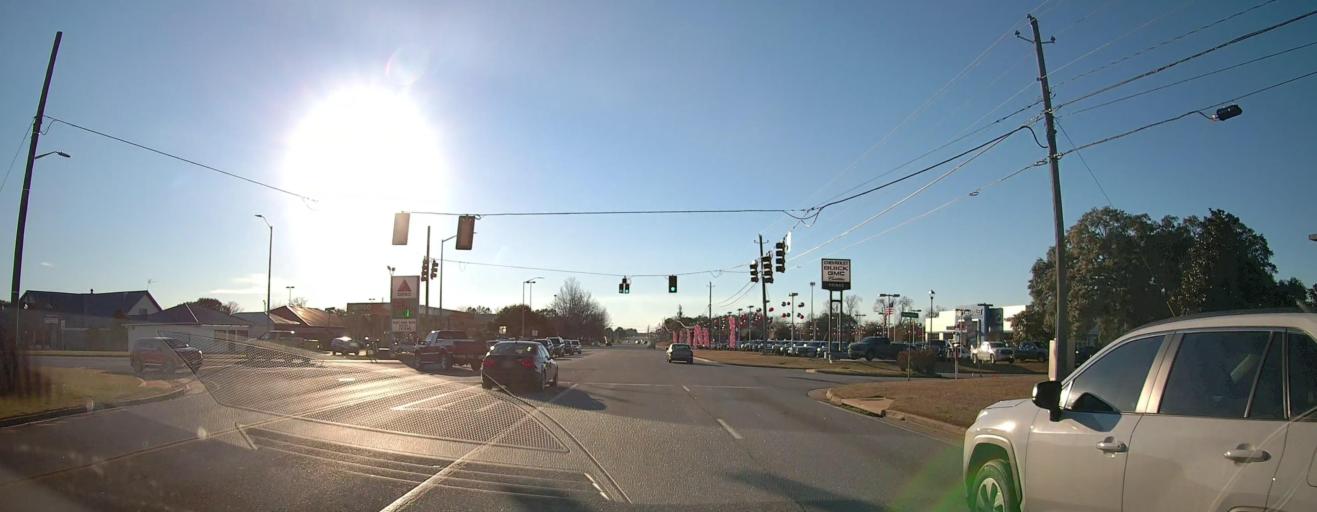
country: US
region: Georgia
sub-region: Dougherty County
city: Albany
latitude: 31.6226
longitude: -84.2038
